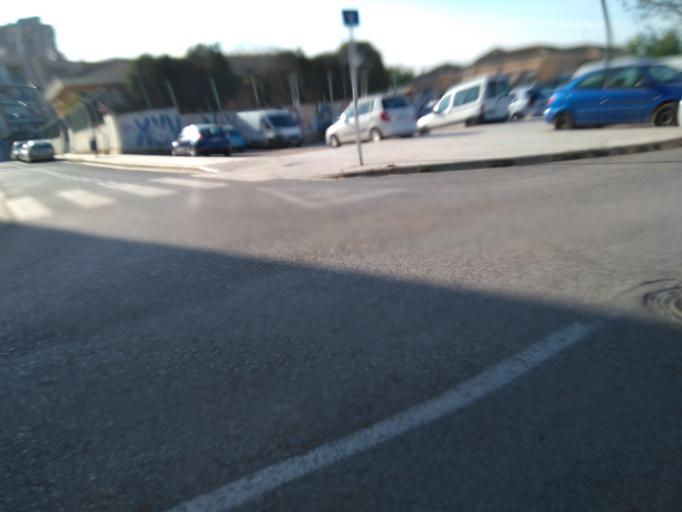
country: ES
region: Valencia
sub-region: Provincia de Valencia
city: Tavernes Blanques
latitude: 39.4977
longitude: -0.3734
